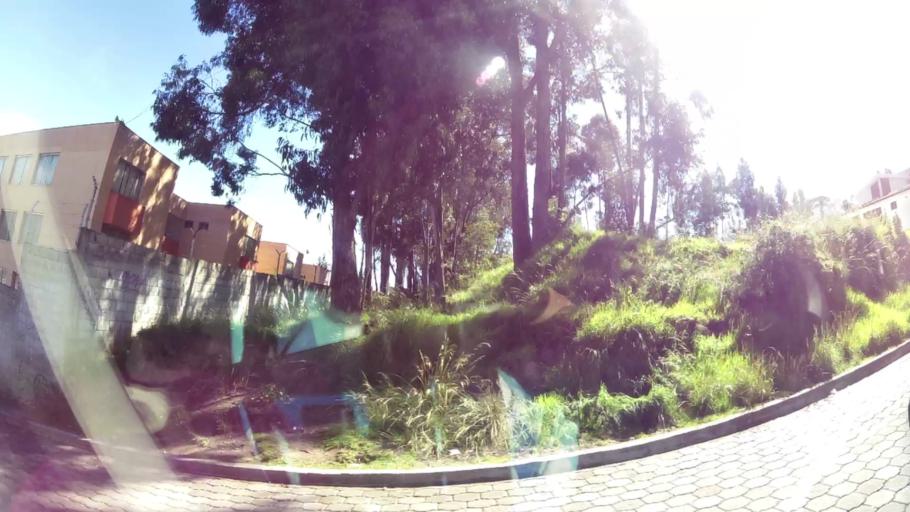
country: EC
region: Pichincha
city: Quito
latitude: -0.1205
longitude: -78.4787
